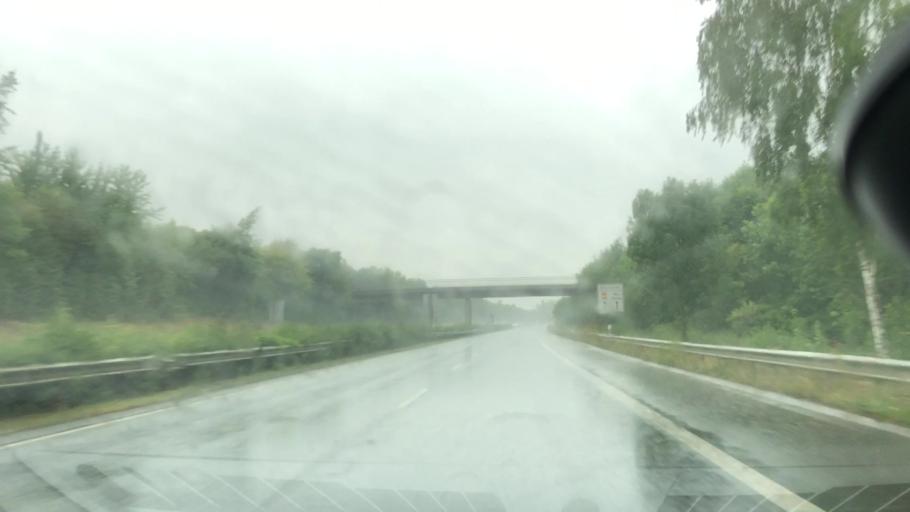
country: DE
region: North Rhine-Westphalia
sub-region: Regierungsbezirk Detmold
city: Minden
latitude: 52.2715
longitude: 8.9082
